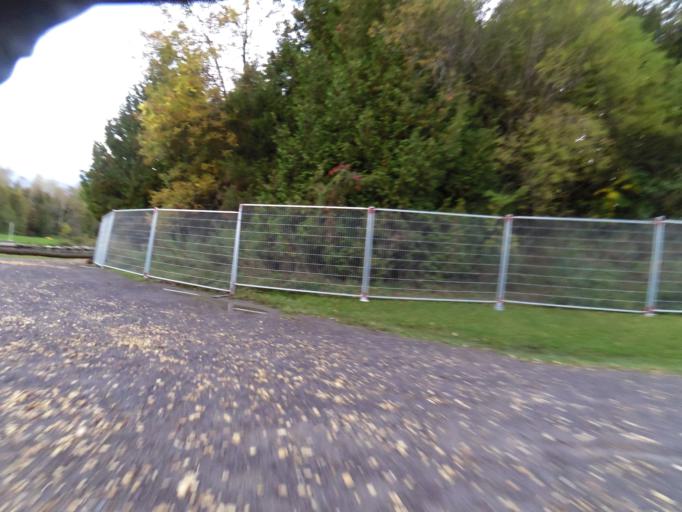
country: CA
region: Ontario
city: Quinte West
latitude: 44.0380
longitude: -77.6590
